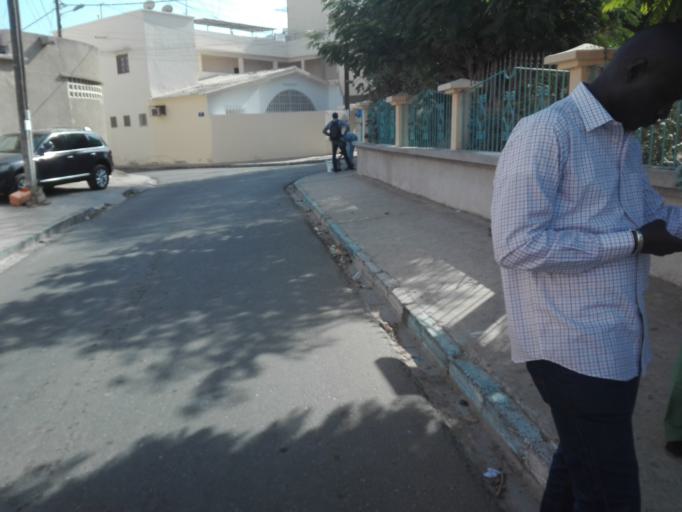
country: SN
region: Dakar
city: Dakar
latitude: 14.6796
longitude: -17.4633
